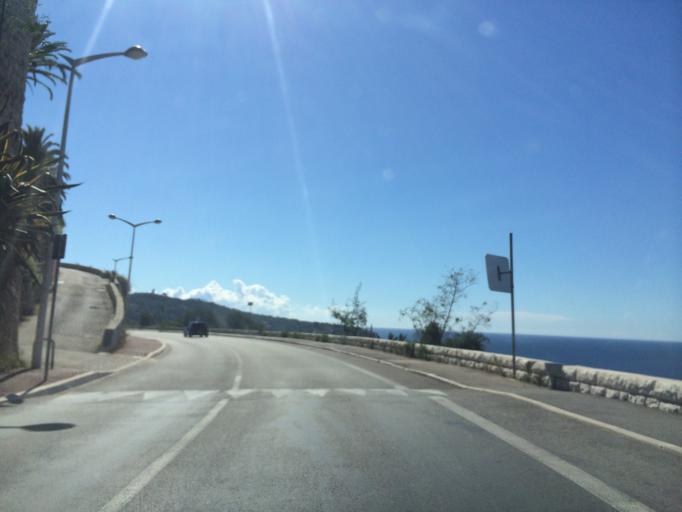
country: FR
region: Provence-Alpes-Cote d'Azur
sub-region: Departement des Alpes-Maritimes
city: Villefranche-sur-Mer
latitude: 43.6864
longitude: 7.3030
